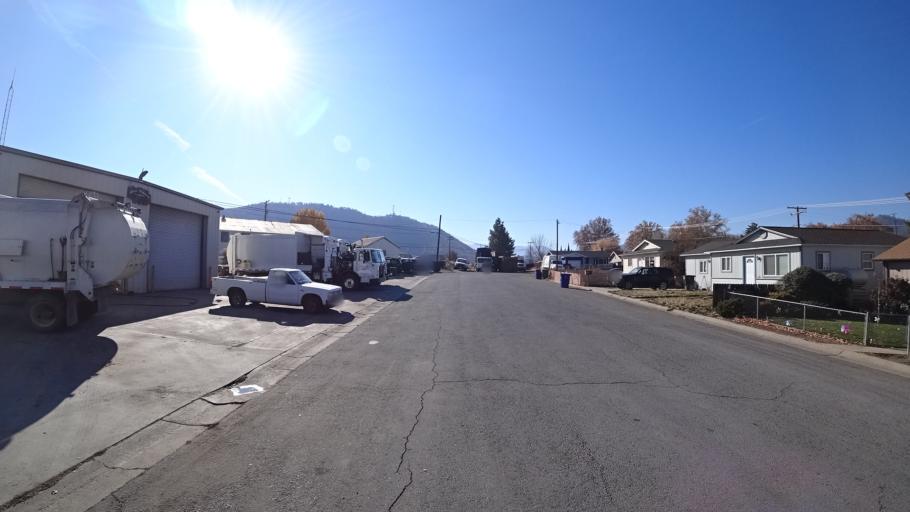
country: US
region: California
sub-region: Siskiyou County
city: Yreka
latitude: 41.7342
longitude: -122.6289
